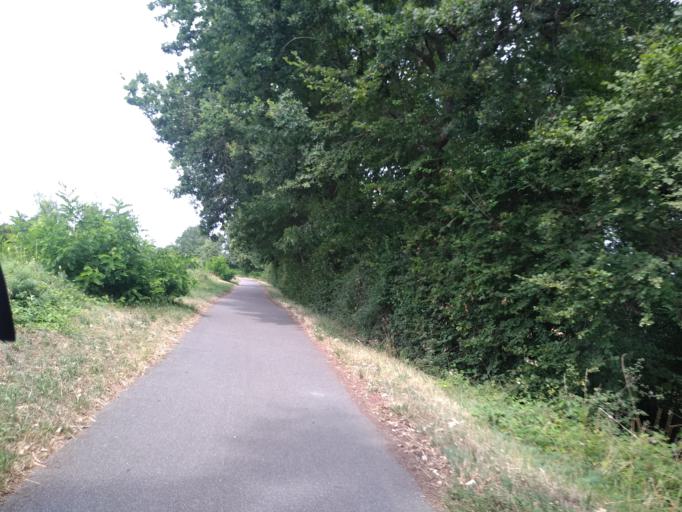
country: FR
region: Auvergne
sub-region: Departement de l'Allier
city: Molinet
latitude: 46.4744
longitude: 3.9354
